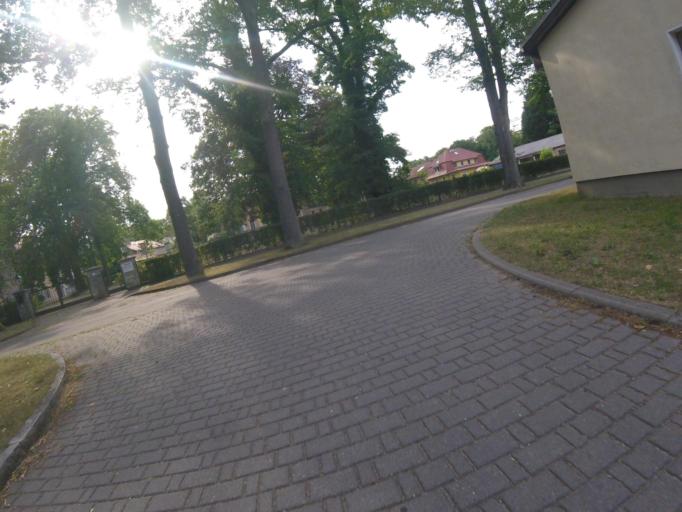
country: DE
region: Brandenburg
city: Munchehofe
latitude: 52.2554
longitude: 13.8000
